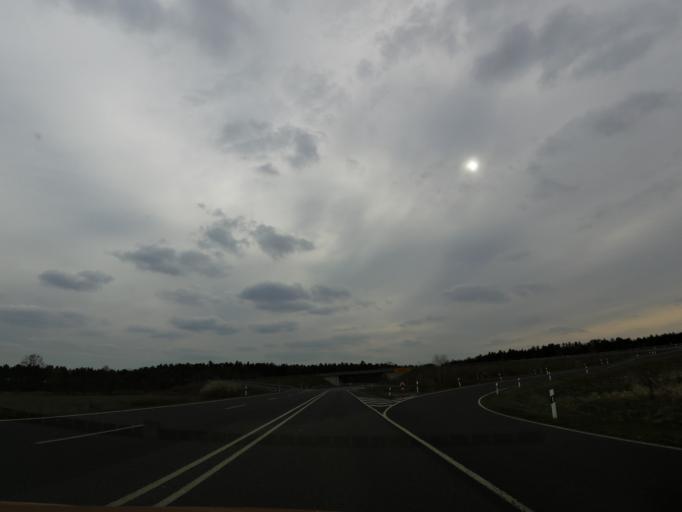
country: DE
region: Brandenburg
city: Mullrose
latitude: 52.2386
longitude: 14.3954
